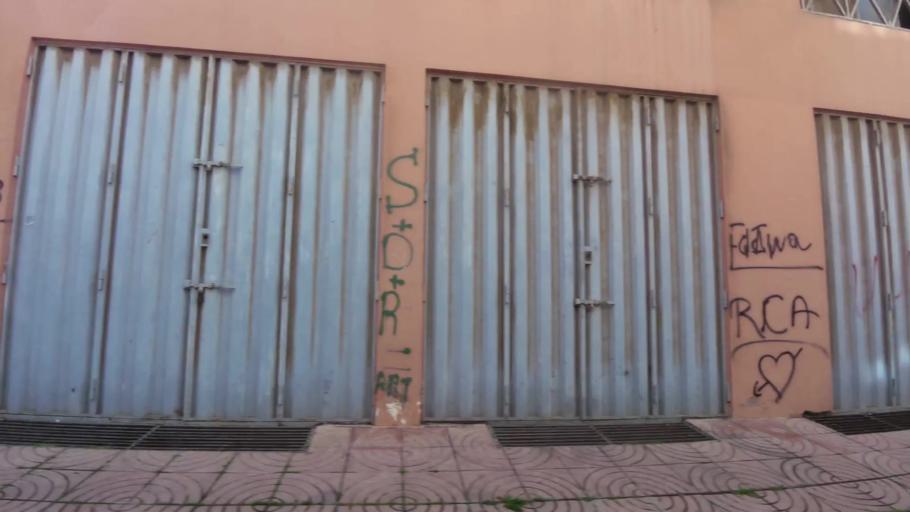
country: MA
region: Grand Casablanca
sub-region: Nouaceur
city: Bouskoura
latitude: 33.5170
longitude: -7.6526
